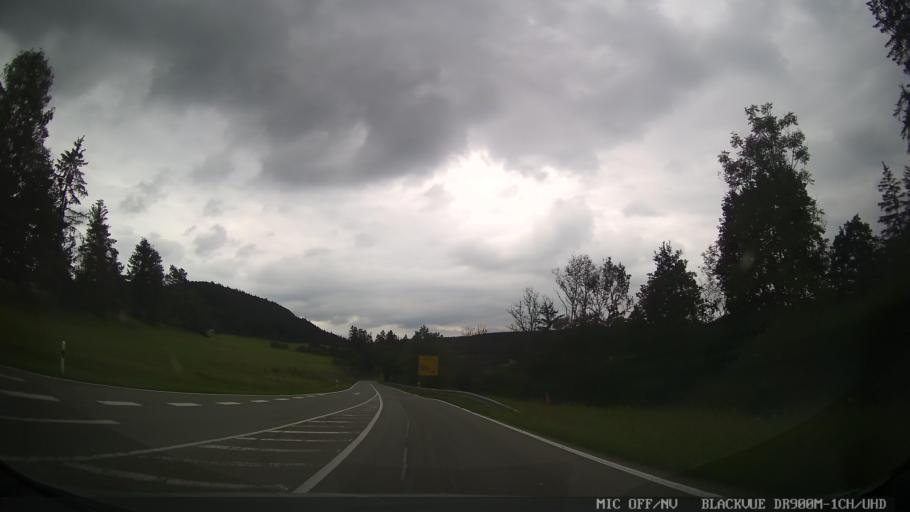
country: DE
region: Baden-Wuerttemberg
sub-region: Freiburg Region
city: Fridingen an der Donau
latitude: 48.0081
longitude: 8.9165
